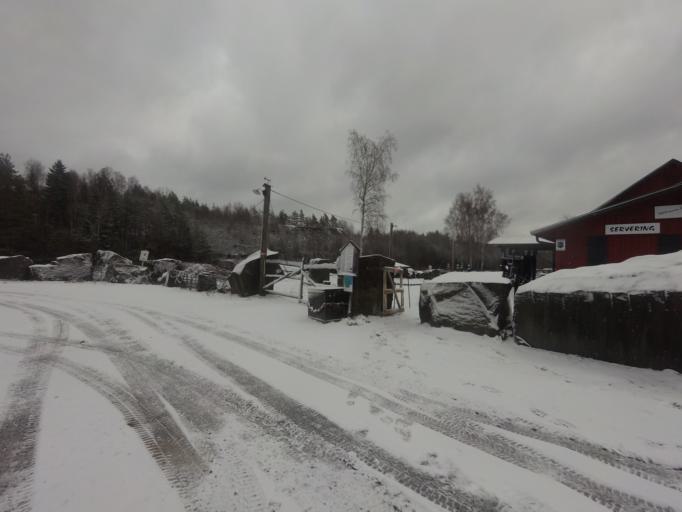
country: SE
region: Skane
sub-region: Osby Kommun
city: Lonsboda
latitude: 56.3950
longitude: 14.2498
